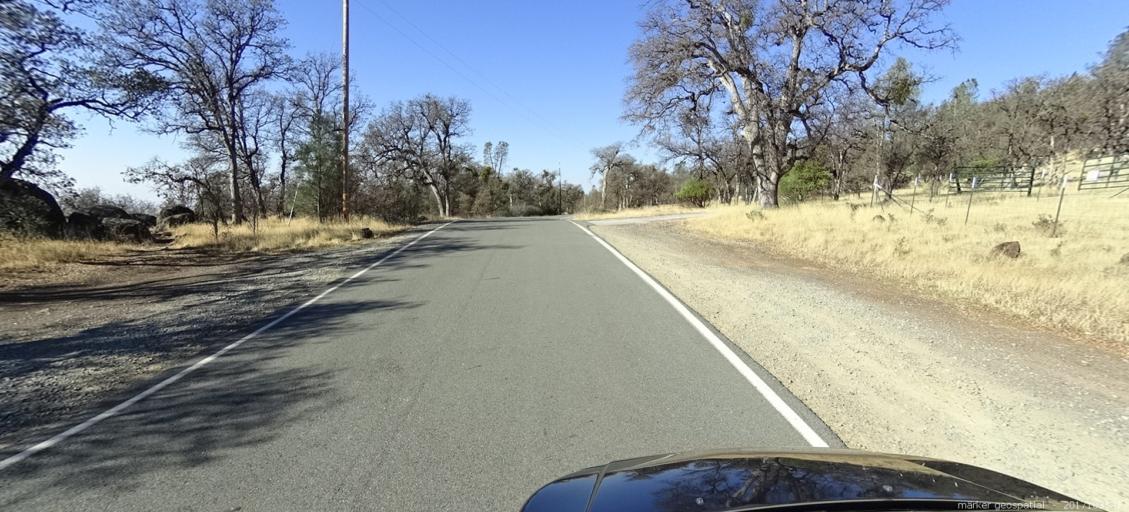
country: US
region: California
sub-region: Shasta County
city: Shingletown
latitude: 40.4712
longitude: -121.8820
